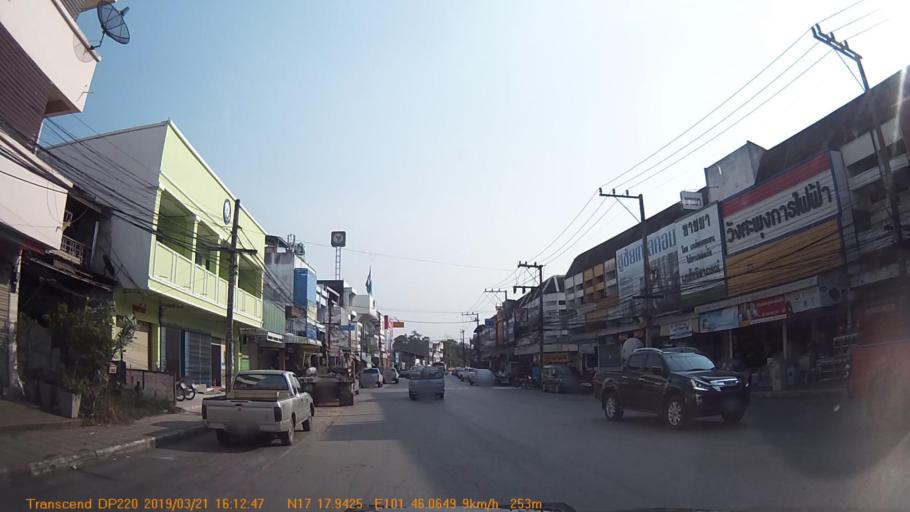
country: TH
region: Loei
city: Wang Saphung
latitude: 17.2990
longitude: 101.7677
